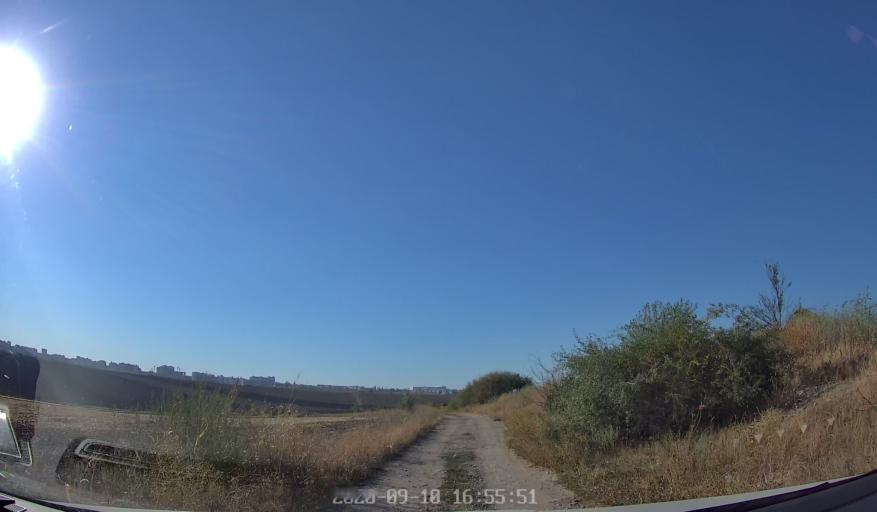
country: MD
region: Chisinau
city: Stauceni
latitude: 47.0548
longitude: 28.9184
